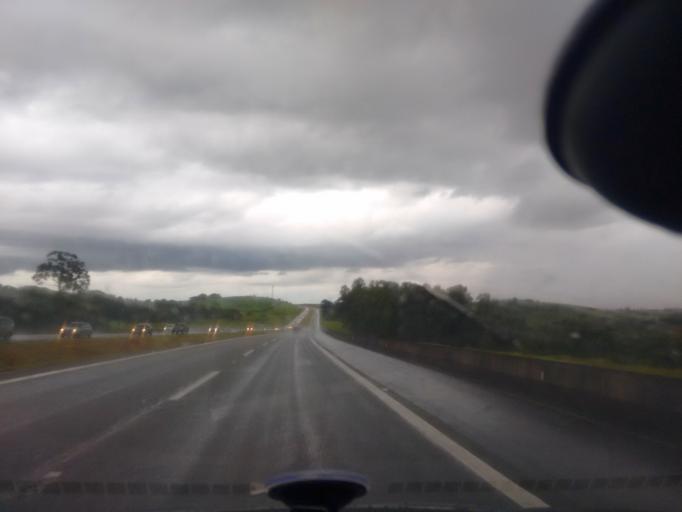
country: BR
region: Sao Paulo
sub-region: Santa Barbara D'Oeste
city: Santa Barbara d'Oeste
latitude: -22.6618
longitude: -47.4491
